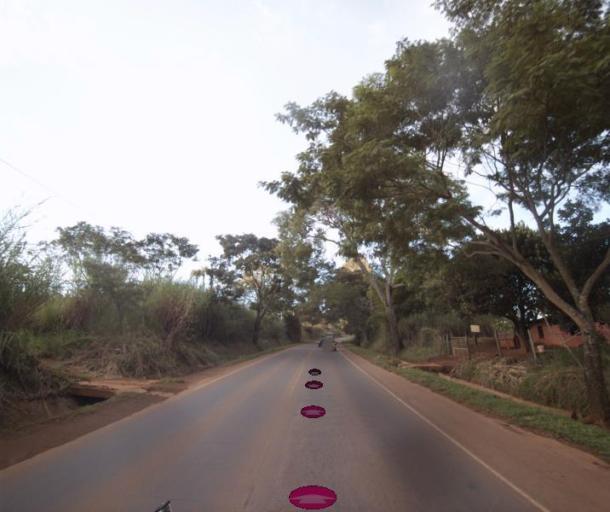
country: BR
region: Goias
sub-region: Anapolis
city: Anapolis
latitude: -16.2405
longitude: -48.9342
